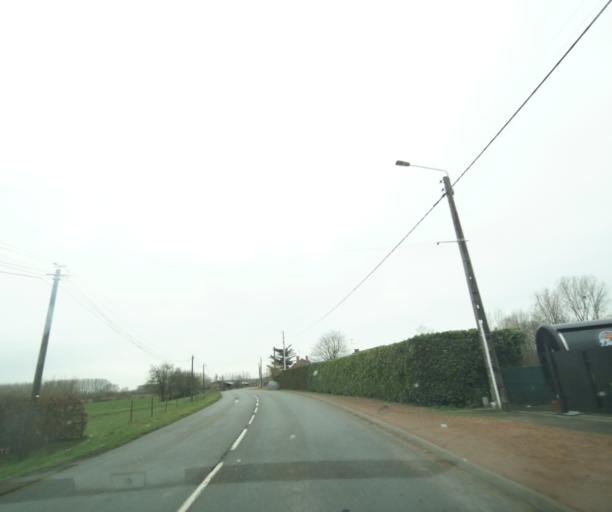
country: BE
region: Wallonia
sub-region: Province du Hainaut
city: Bernissart
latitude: 50.4468
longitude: 3.6477
